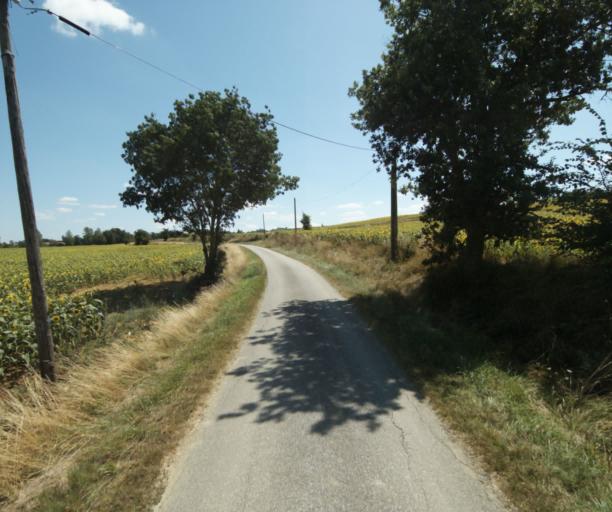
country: FR
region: Midi-Pyrenees
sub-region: Departement de la Haute-Garonne
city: Saint-Felix-Lauragais
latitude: 43.4694
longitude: 1.8857
